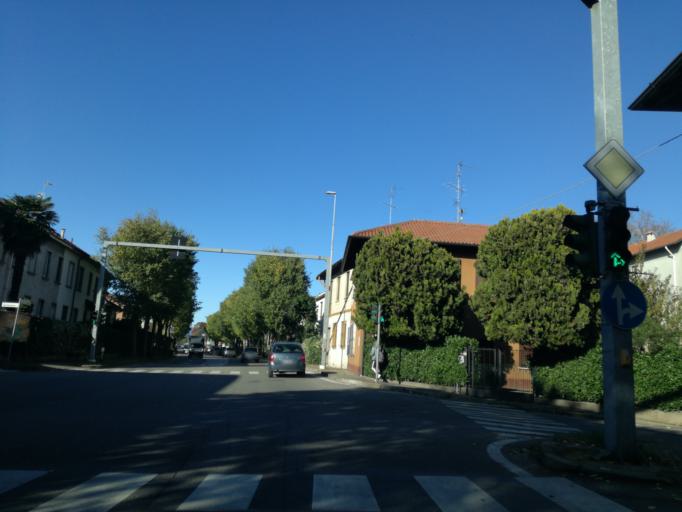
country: IT
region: Lombardy
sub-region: Provincia di Monza e Brianza
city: Sovico
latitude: 45.6477
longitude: 9.2602
